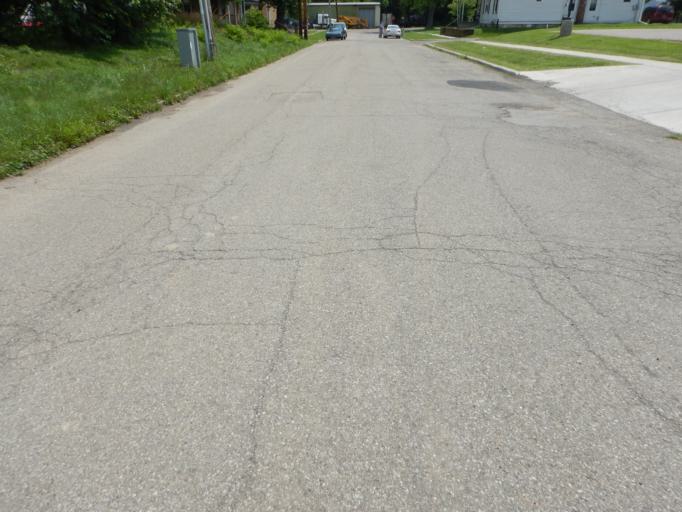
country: US
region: Ohio
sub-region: Muskingum County
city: Zanesville
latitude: 39.9249
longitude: -82.0051
